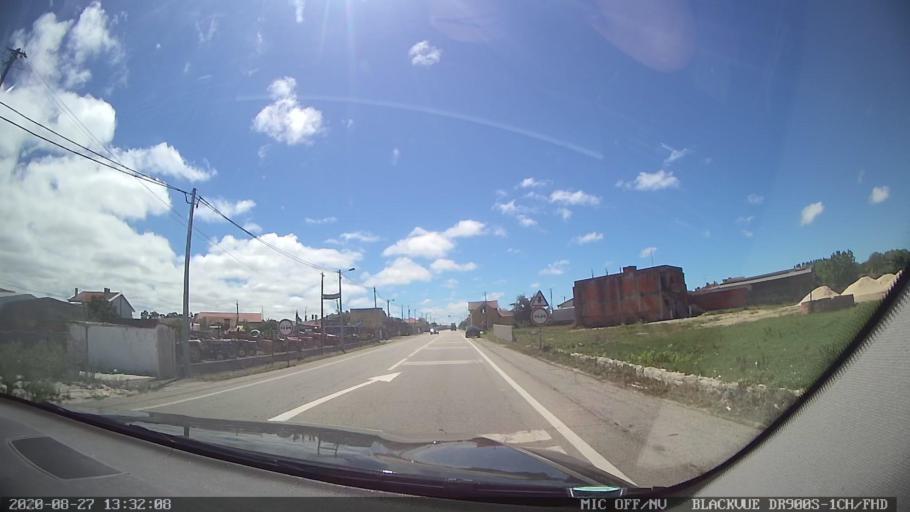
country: PT
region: Aveiro
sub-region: Vagos
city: Vagos
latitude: 40.4901
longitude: -8.6865
